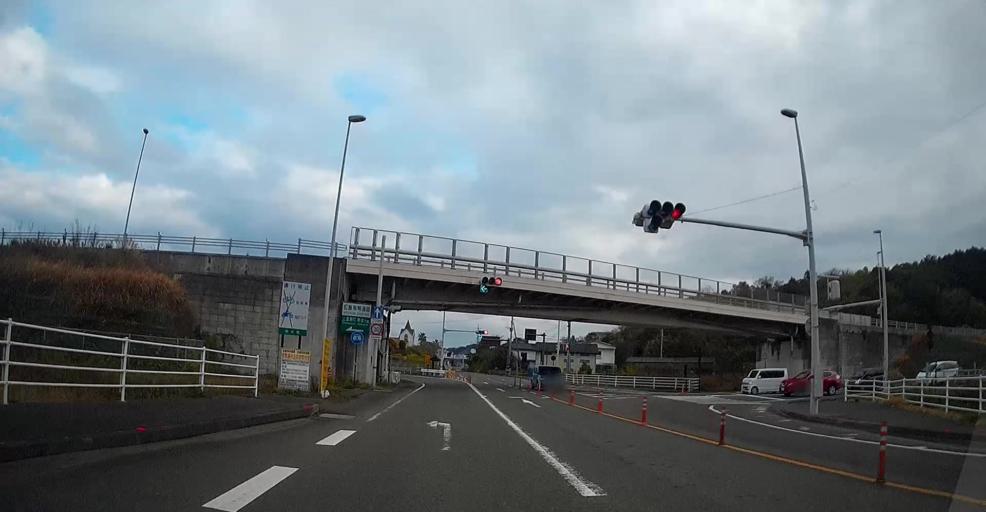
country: JP
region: Kumamoto
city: Hondo
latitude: 32.5045
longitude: 130.3030
